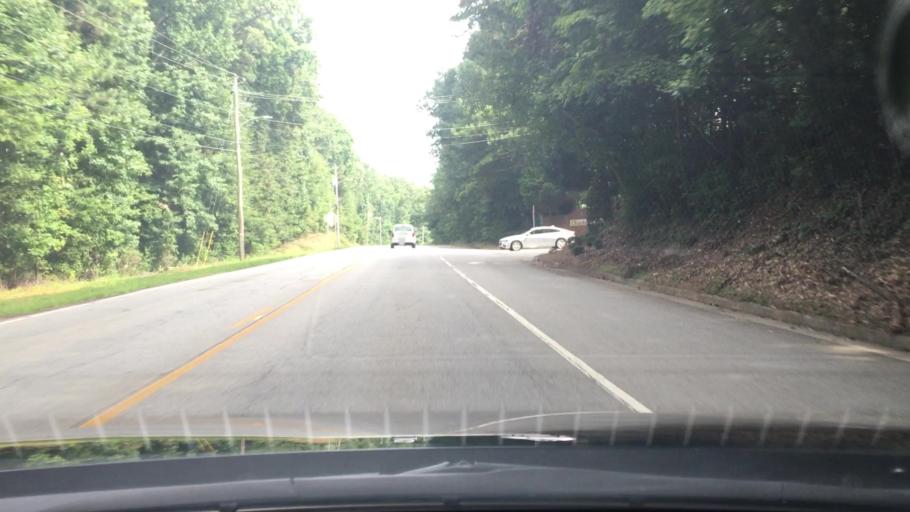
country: US
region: Georgia
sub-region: Coweta County
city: Newnan
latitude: 33.3754
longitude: -84.7790
